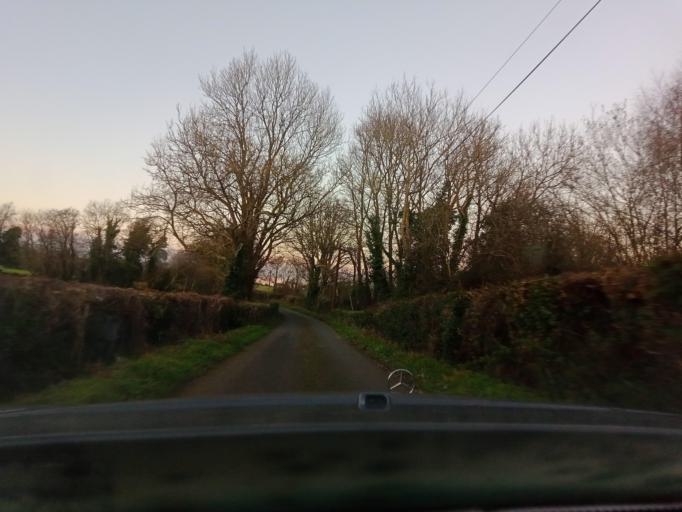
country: IE
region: Leinster
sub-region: Kilkenny
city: Graiguenamanagh
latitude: 52.5677
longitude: -6.9585
